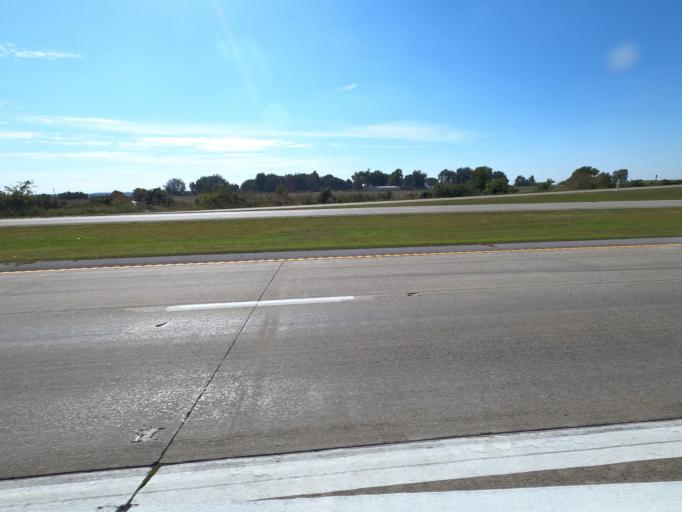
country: US
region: Missouri
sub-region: Pemiscot County
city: Caruthersville
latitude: 36.1503
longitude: -89.6602
